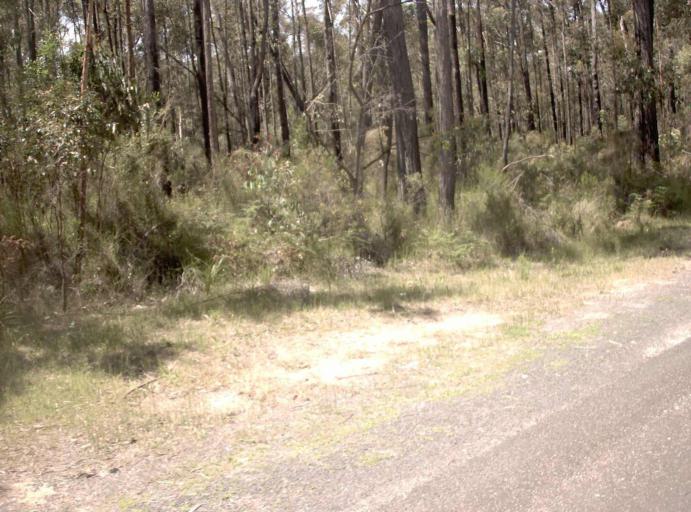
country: AU
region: New South Wales
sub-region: Bombala
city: Bombala
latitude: -37.5647
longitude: 149.0524
